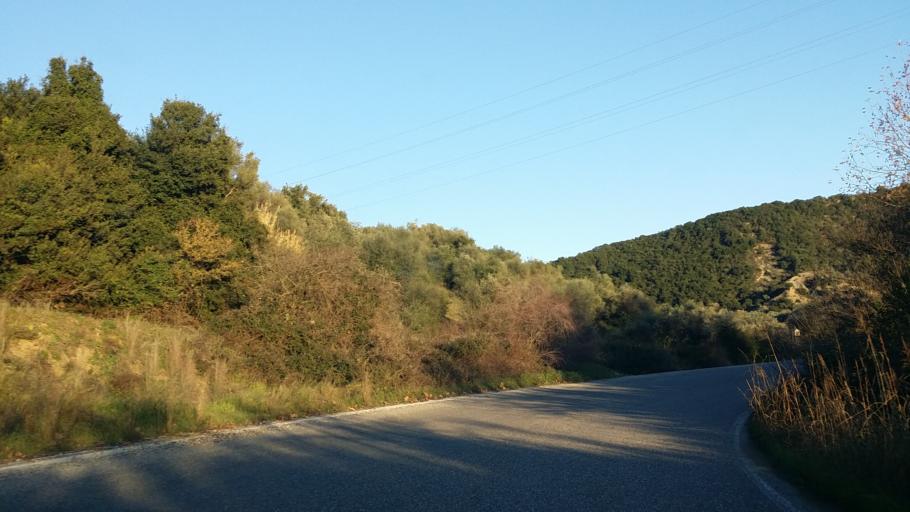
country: GR
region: West Greece
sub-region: Nomos Aitolias kai Akarnanias
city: Neapolis
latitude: 38.7100
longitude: 21.3485
